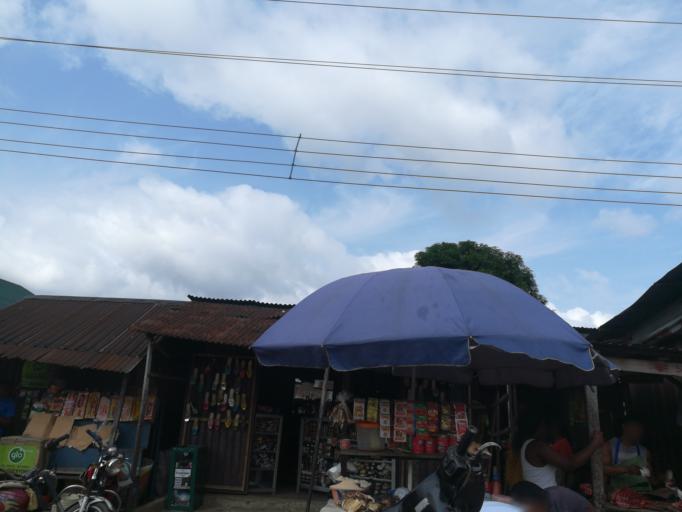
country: NG
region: Rivers
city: Okrika
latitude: 4.7502
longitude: 7.0998
